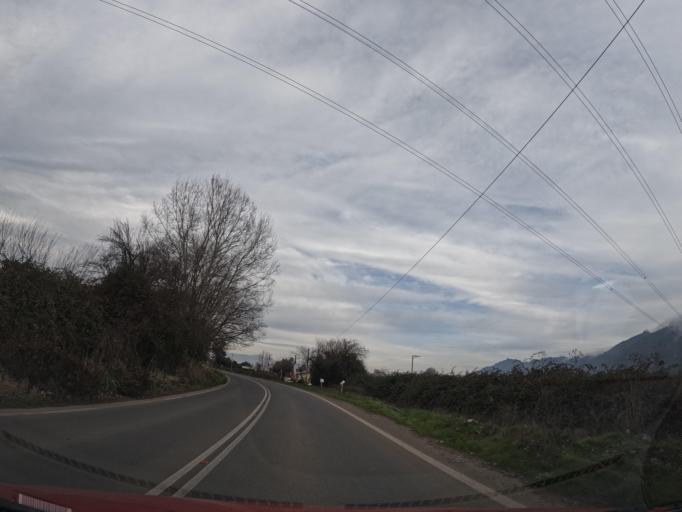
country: CL
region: Maule
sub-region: Provincia de Linares
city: Colbun
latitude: -35.5803
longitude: -71.3192
